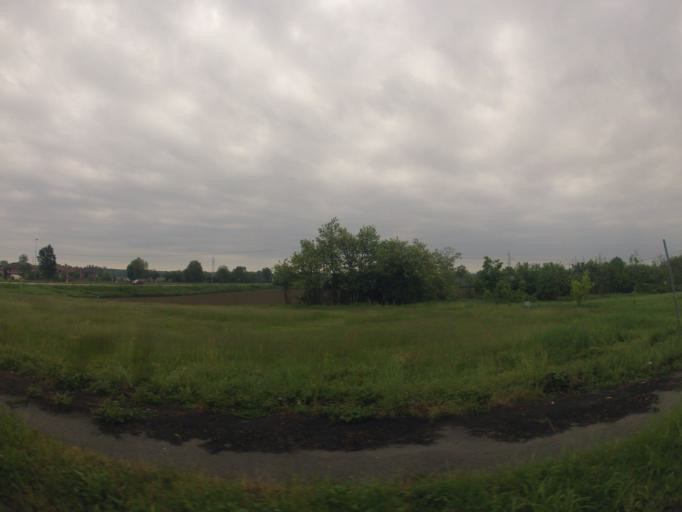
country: IT
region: Piedmont
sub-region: Provincia di Torino
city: Carignano
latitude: 44.8912
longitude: 7.6689
